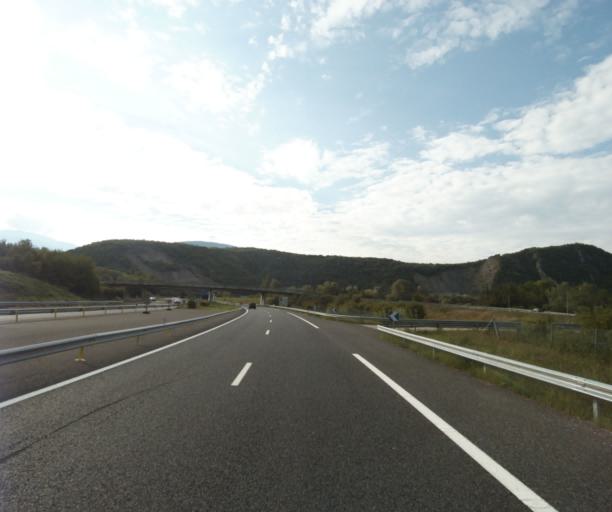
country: FR
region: Rhone-Alpes
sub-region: Departement de l'Isere
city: Allieres-et-Risset
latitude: 45.0873
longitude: 5.6703
